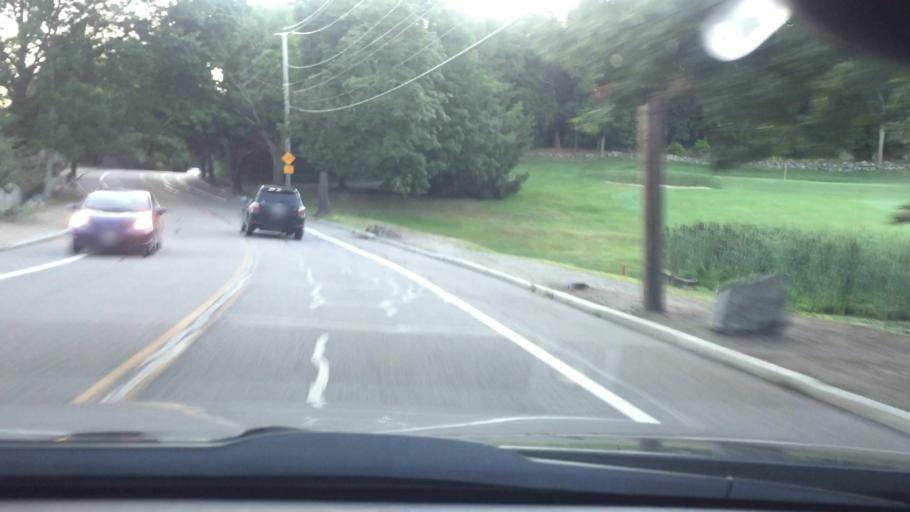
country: US
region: Massachusetts
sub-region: Middlesex County
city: Newton
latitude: 42.3000
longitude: -71.1915
